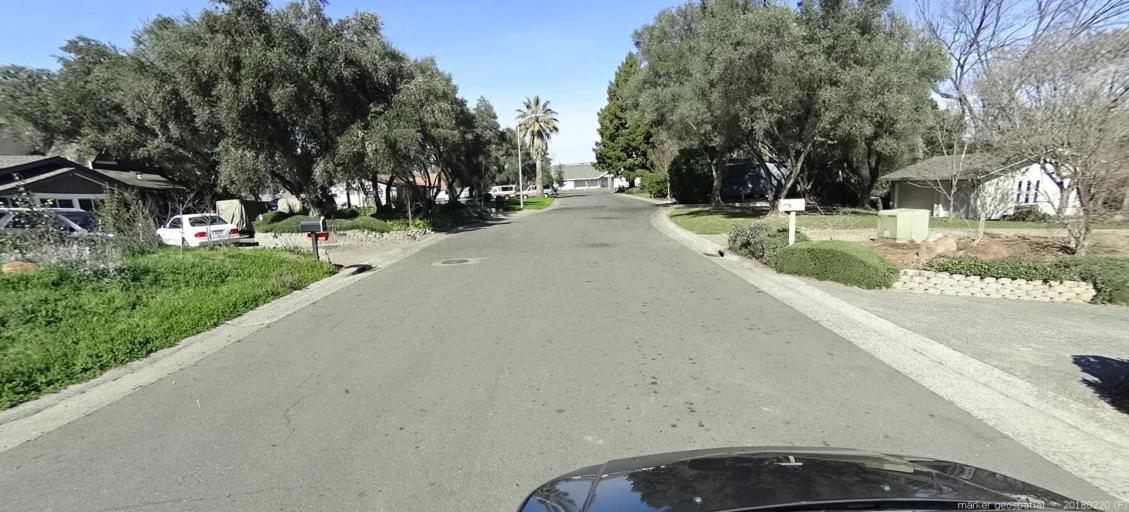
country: US
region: California
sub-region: Sacramento County
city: Orangevale
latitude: 38.6918
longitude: -121.2128
